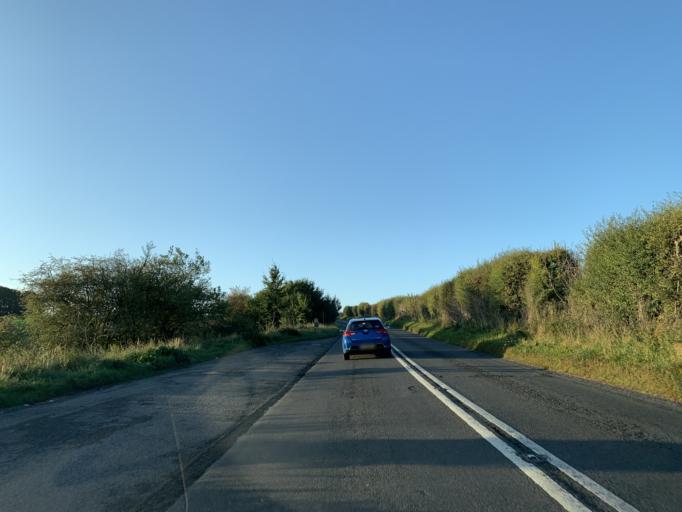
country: GB
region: England
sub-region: Wiltshire
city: Woodford
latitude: 51.1389
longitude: -1.8582
